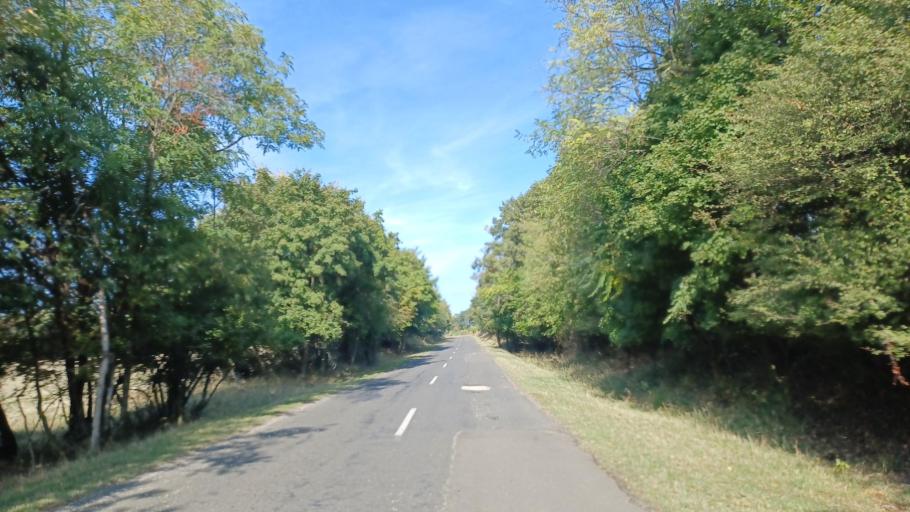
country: HU
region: Tolna
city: Pincehely
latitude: 46.6678
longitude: 18.4787
